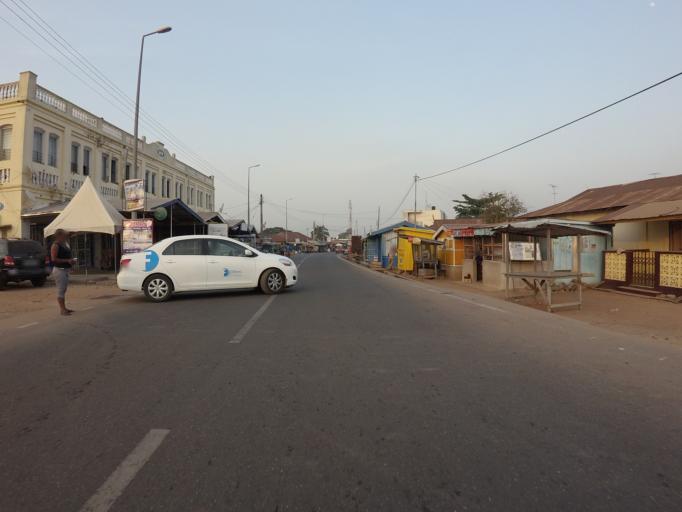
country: GH
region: Volta
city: Ho
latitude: 6.6059
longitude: 0.4717
